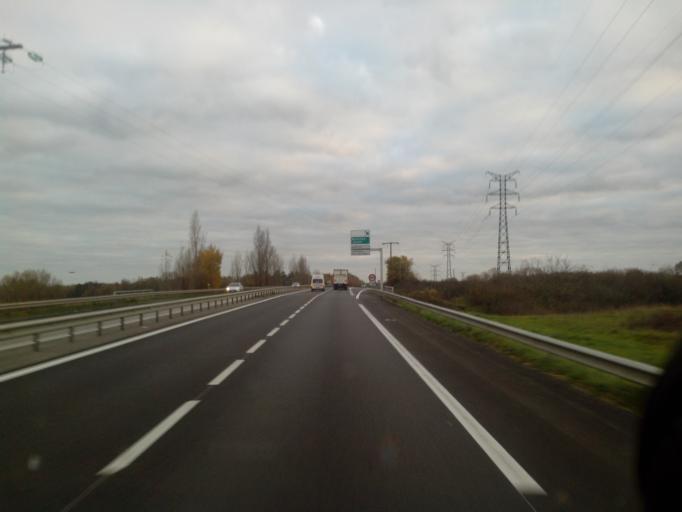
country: FR
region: Poitou-Charentes
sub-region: Departement de la Vienne
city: Mignaloux-Beauvoir
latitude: 46.5777
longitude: 0.3963
